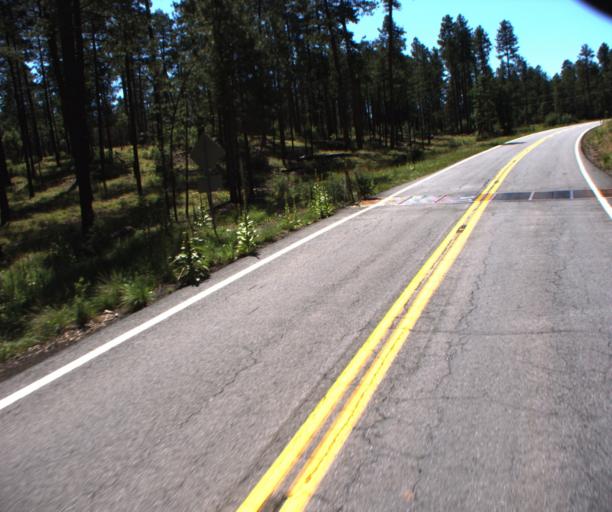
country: US
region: Arizona
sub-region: Apache County
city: Eagar
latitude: 33.7319
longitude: -109.2031
